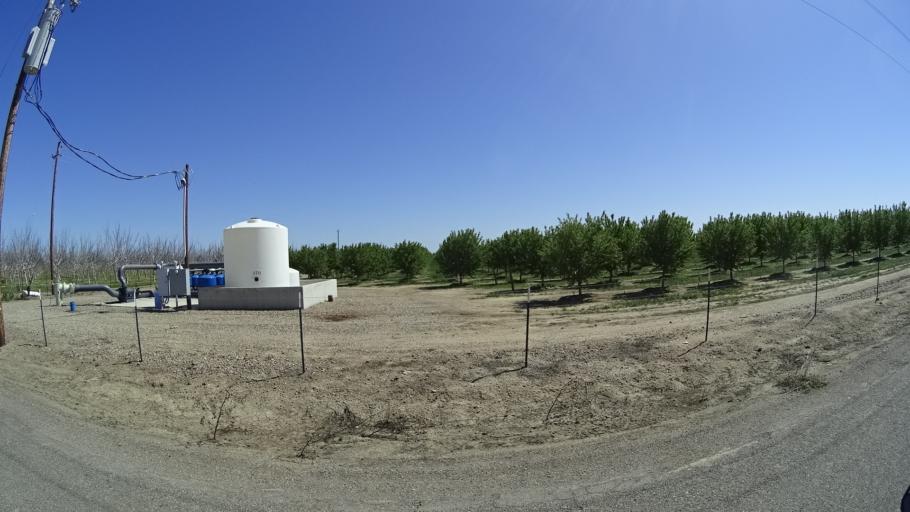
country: US
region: California
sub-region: Glenn County
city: Orland
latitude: 39.6825
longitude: -122.2342
